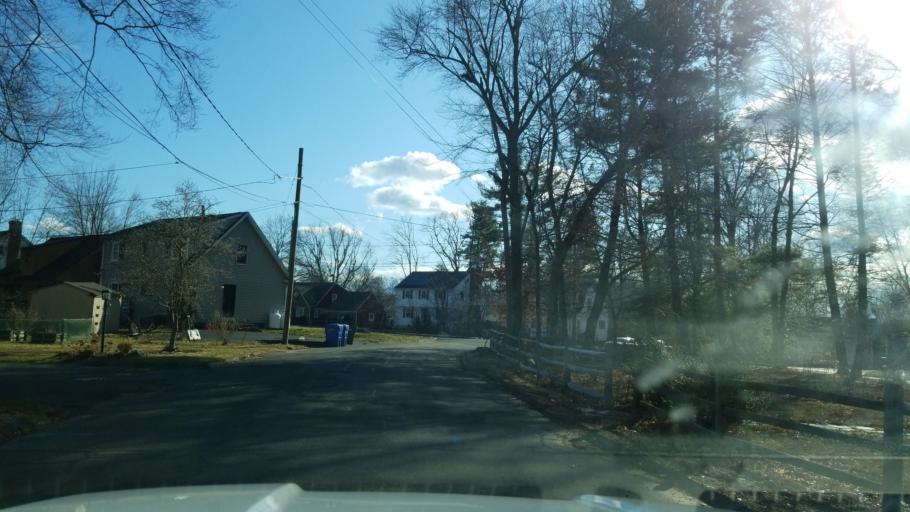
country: US
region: Connecticut
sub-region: Middlesex County
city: Middletown
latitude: 41.5603
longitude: -72.6770
